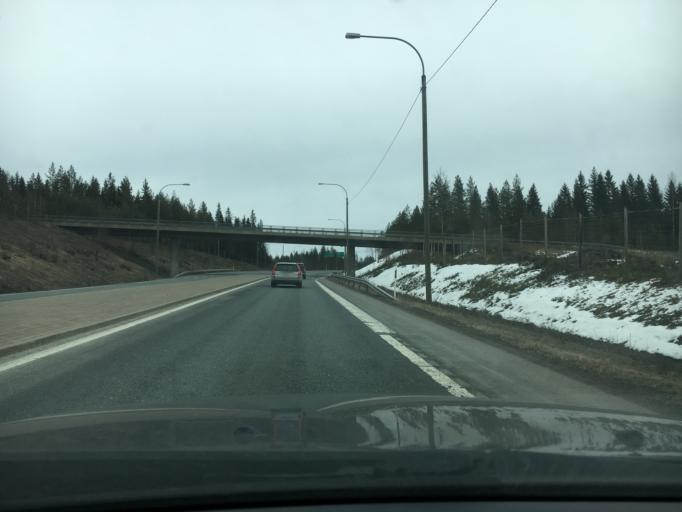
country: FI
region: Northern Savo
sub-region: Kuopio
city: Kuopio
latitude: 62.7159
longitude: 27.5655
